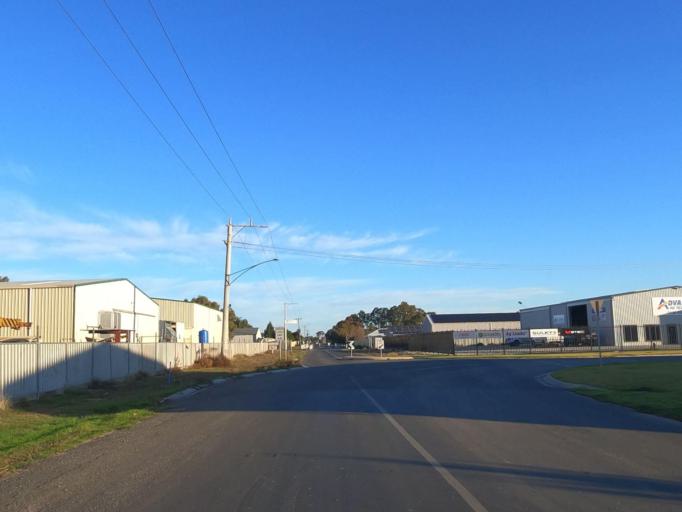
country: AU
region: Victoria
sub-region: Swan Hill
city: Swan Hill
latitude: -35.3278
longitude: 143.5350
